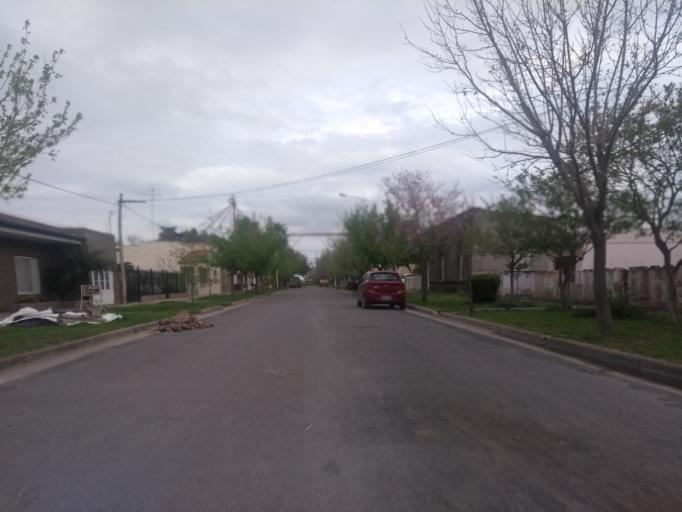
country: AR
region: Santa Fe
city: Galvez
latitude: -31.9057
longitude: -61.2789
